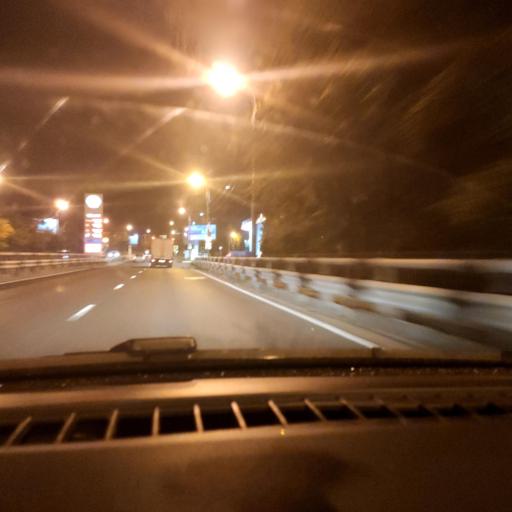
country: RU
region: Voronezj
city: Voronezh
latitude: 51.6946
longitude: 39.2204
